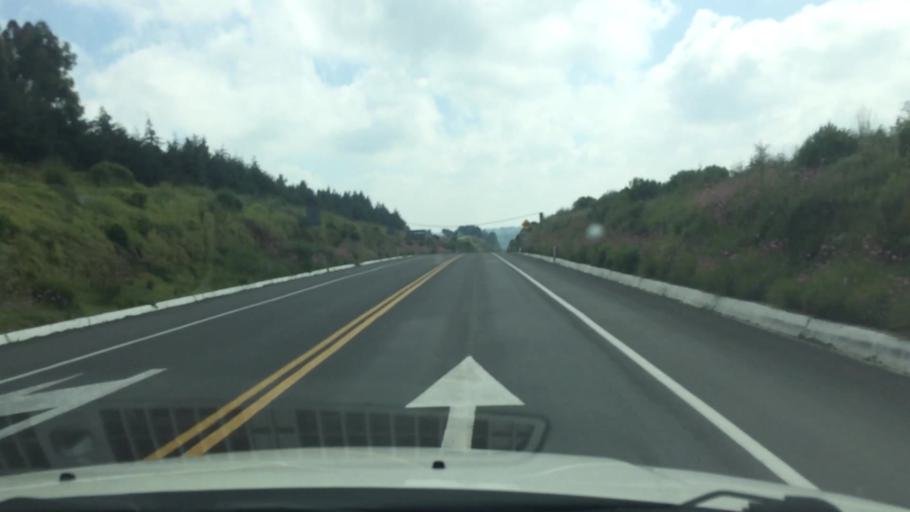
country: MX
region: Mexico
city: Amanalco de Becerra
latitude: 19.3548
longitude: -99.9808
